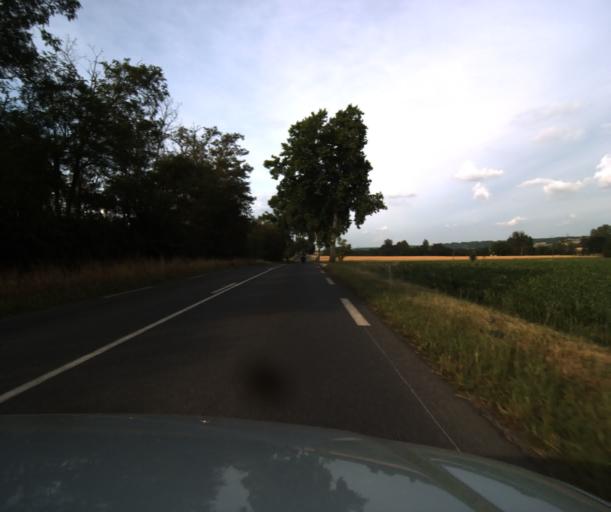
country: FR
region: Midi-Pyrenees
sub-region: Departement du Tarn-et-Garonne
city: Beaumont-de-Lomagne
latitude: 43.9114
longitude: 1.0485
